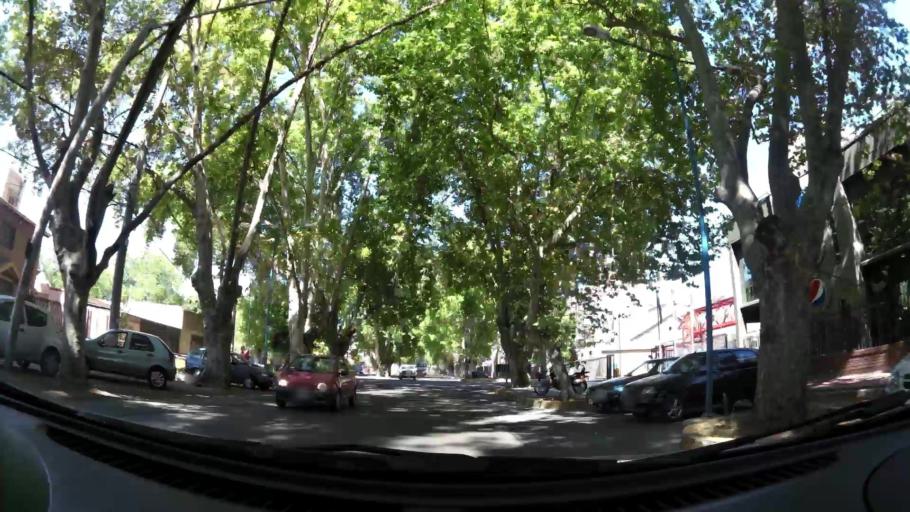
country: AR
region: Mendoza
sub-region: Departamento de Godoy Cruz
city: Godoy Cruz
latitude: -32.9515
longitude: -68.8458
